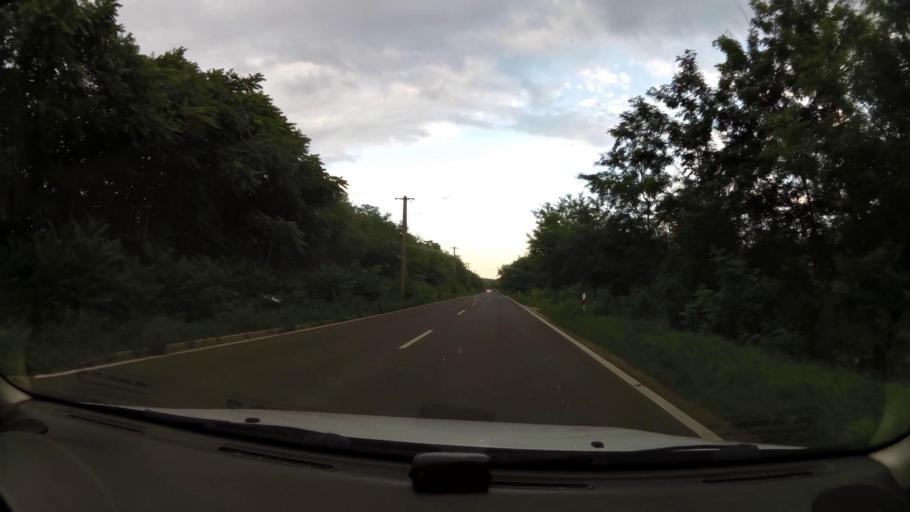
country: HU
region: Pest
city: Tapioszele
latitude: 47.3092
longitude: 19.8778
